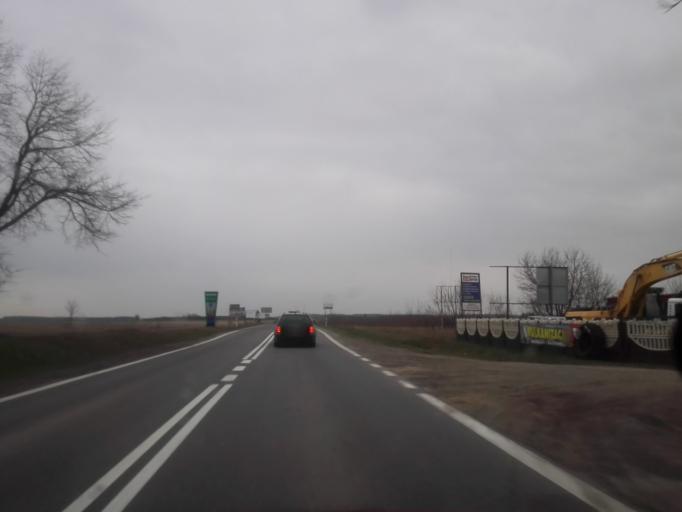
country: PL
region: Podlasie
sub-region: Powiat grajewski
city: Grajewo
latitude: 53.6390
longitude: 22.4369
